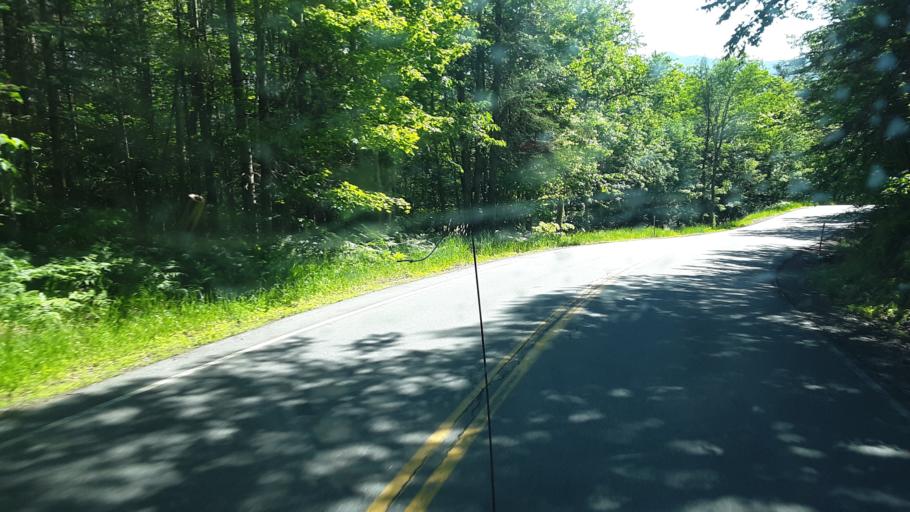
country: US
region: New Hampshire
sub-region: Grafton County
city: North Haverhill
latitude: 44.0984
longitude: -71.8552
